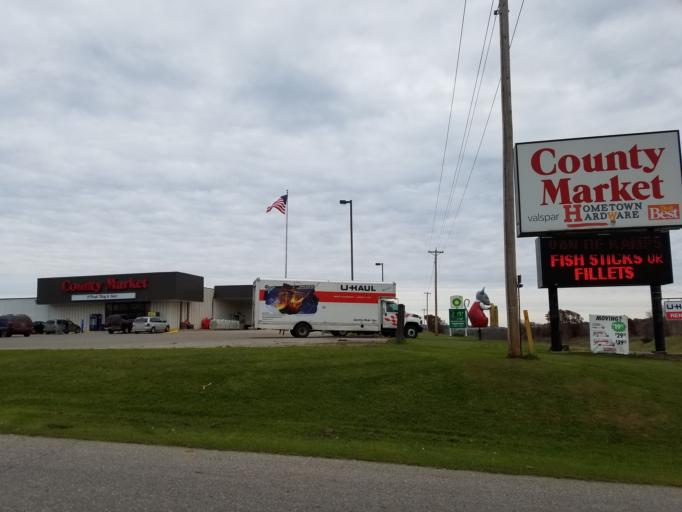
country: US
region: Wisconsin
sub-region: Vernon County
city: Hillsboro
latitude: 43.6605
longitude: -90.3282
